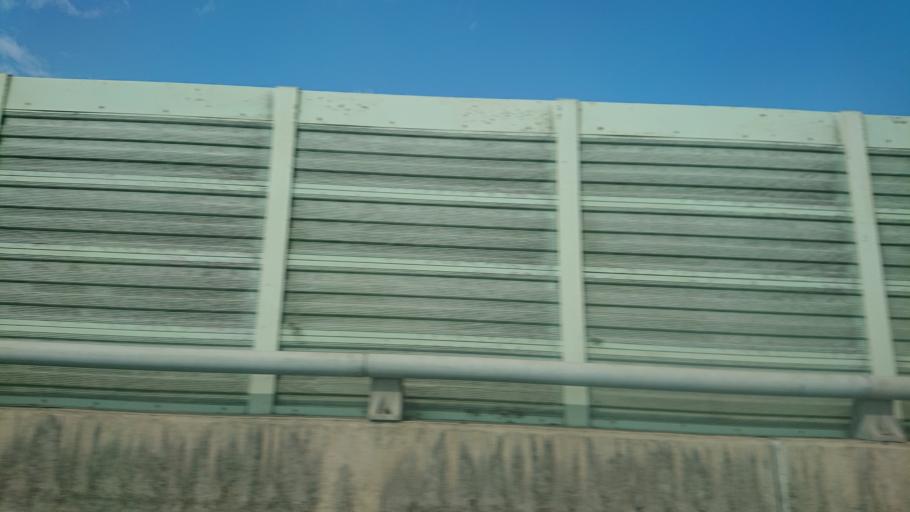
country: TW
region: Taiwan
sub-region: Changhua
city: Chang-hua
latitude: 24.0672
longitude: 120.4125
